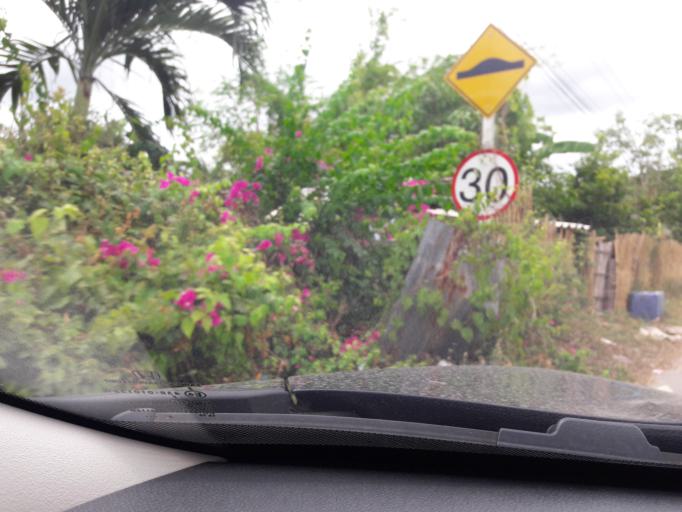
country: TH
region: Ratchaburi
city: Bang Phae
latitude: 13.6026
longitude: 99.9058
